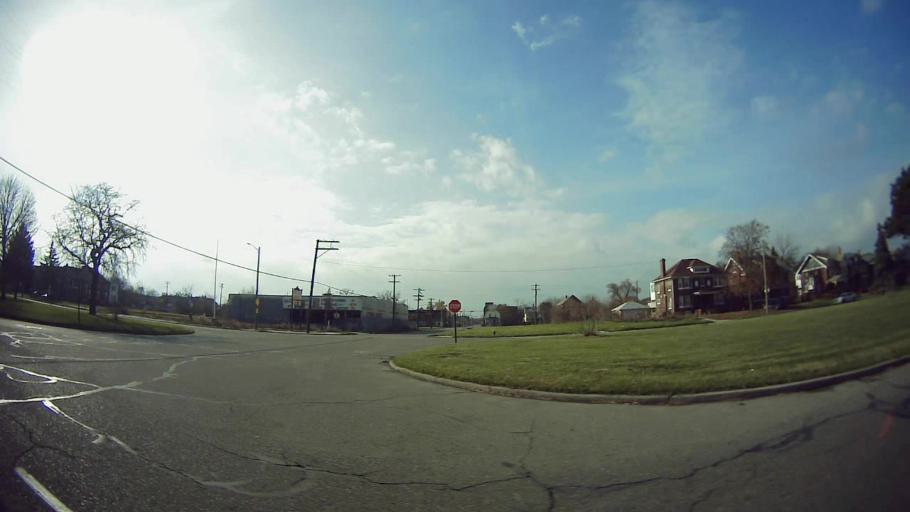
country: US
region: Michigan
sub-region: Wayne County
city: Highland Park
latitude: 42.3501
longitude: -83.1102
